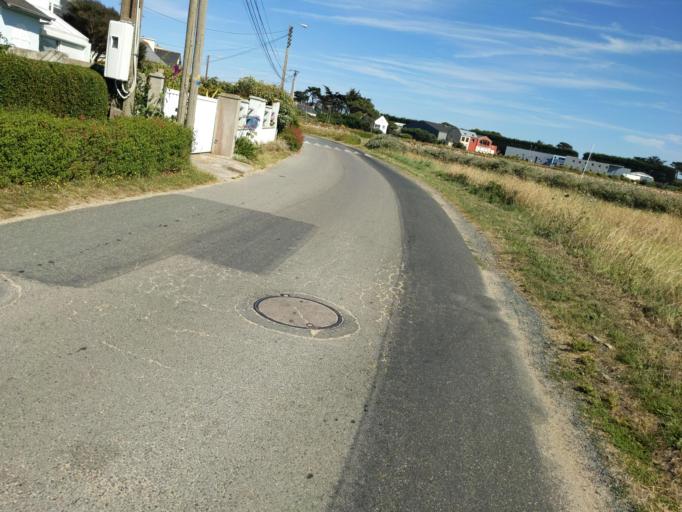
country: FR
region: Brittany
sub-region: Departement des Cotes-d'Armor
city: Pleubian
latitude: 48.8605
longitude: -3.0814
